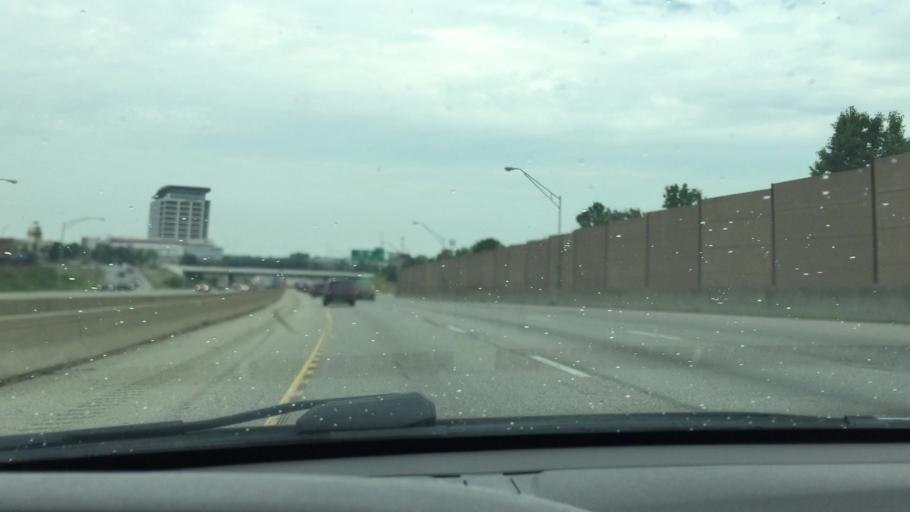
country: US
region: Ohio
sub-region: Hamilton County
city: Madeira
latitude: 39.1977
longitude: -84.3756
